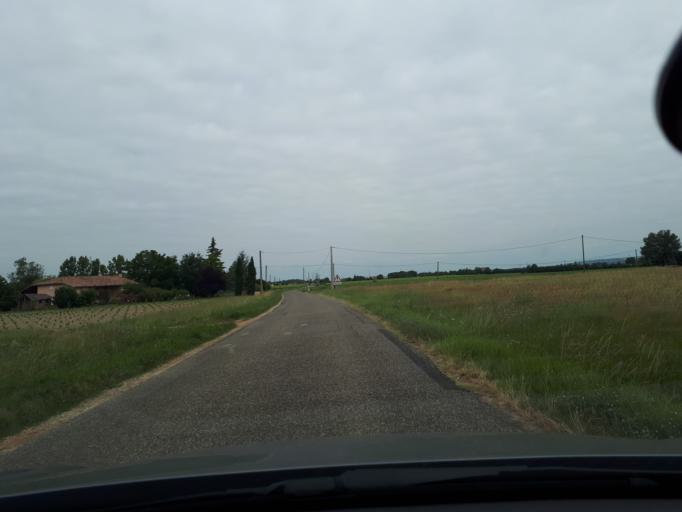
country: FR
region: Midi-Pyrenees
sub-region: Departement du Tarn-et-Garonne
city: Campsas
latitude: 43.8750
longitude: 1.3407
